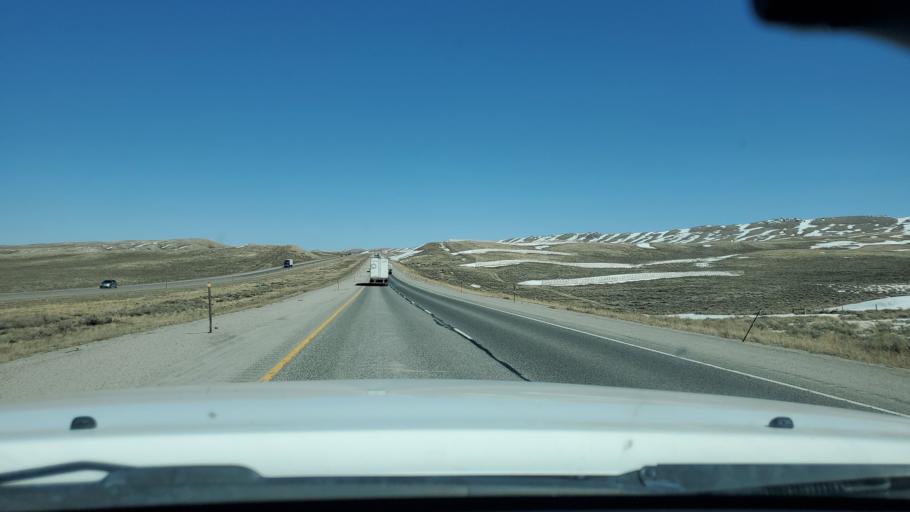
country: US
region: Wyoming
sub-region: Carbon County
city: Saratoga
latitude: 41.7376
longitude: -106.5925
